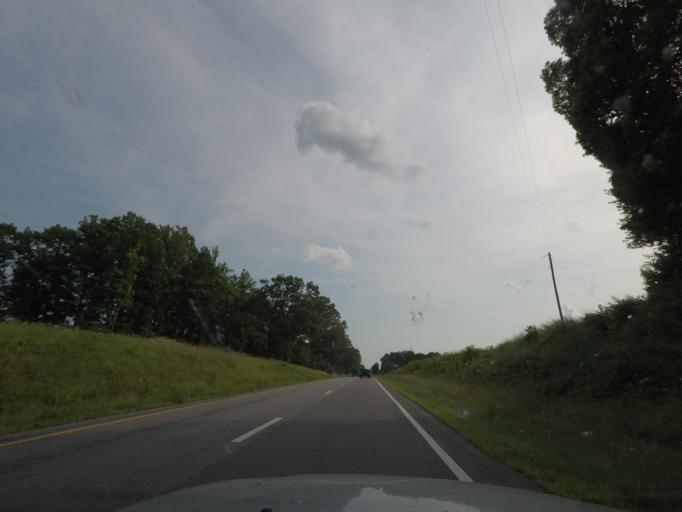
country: US
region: Virginia
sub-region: Mecklenburg County
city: Chase City
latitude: 36.8811
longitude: -78.5594
